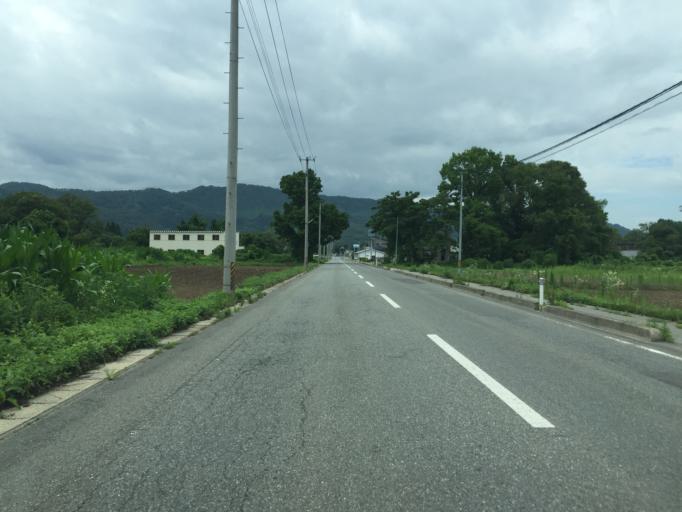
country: JP
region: Yamagata
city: Yonezawa
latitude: 37.8816
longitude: 140.1180
